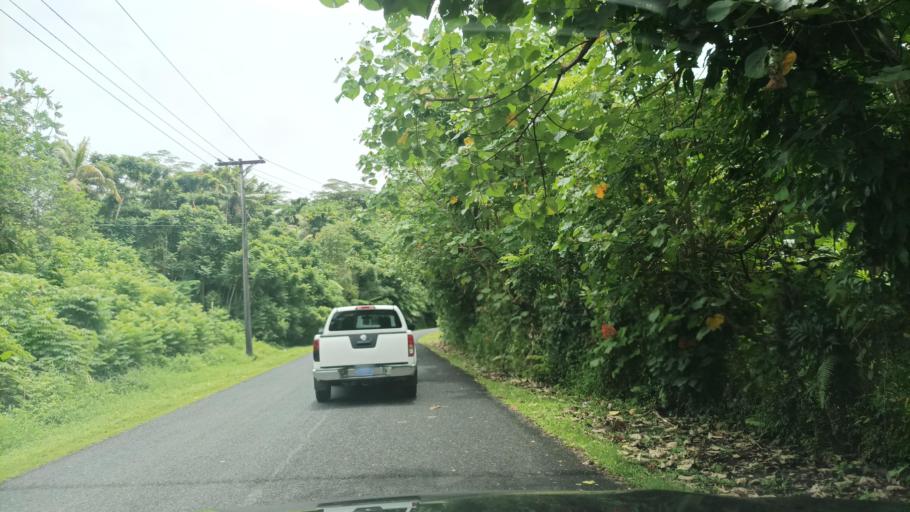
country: FM
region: Pohnpei
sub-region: Sokehs Municipality
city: Palikir - National Government Center
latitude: 6.9242
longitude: 158.1707
